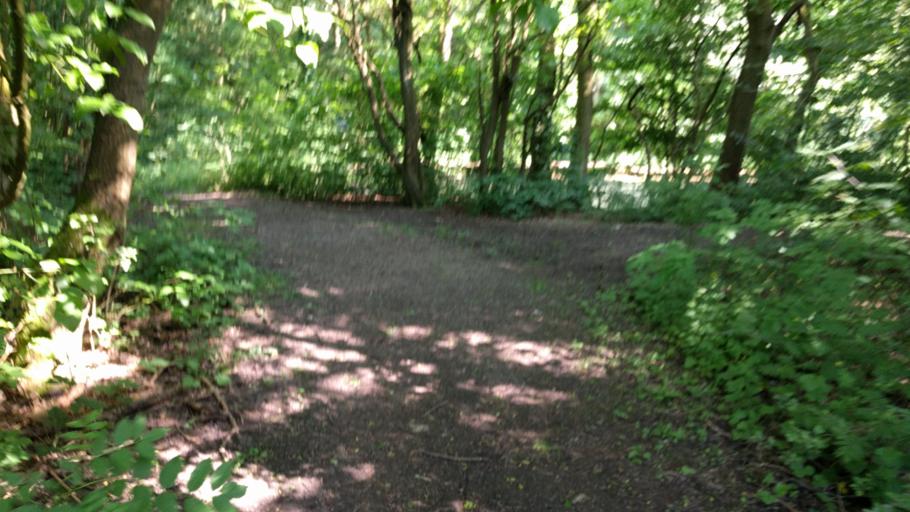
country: GB
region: England
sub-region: Warrington
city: Croft
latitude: 53.4193
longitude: -2.5312
